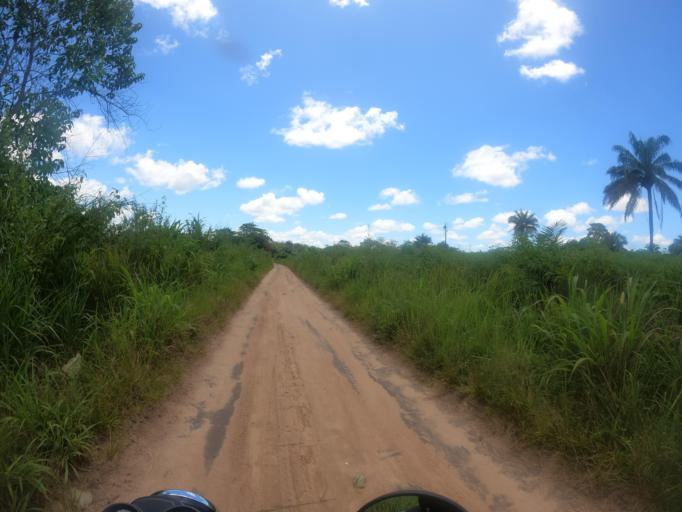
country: SL
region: Northern Province
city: Makeni
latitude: 8.8559
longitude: -12.1133
